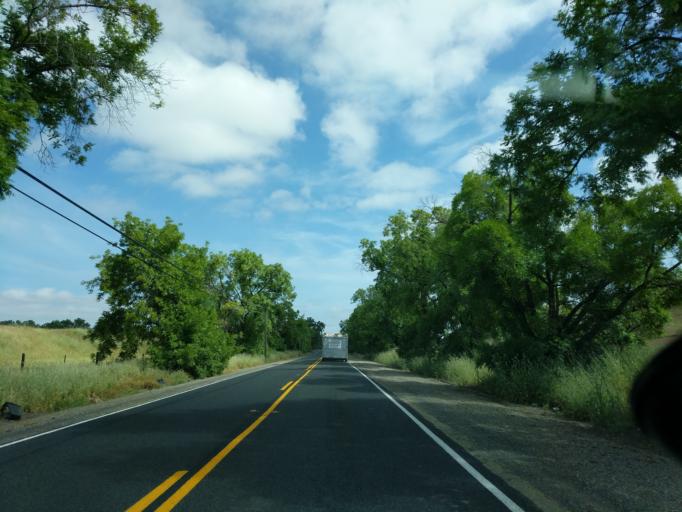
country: US
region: California
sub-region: Contra Costa County
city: Brentwood
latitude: 37.8825
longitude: -121.7236
